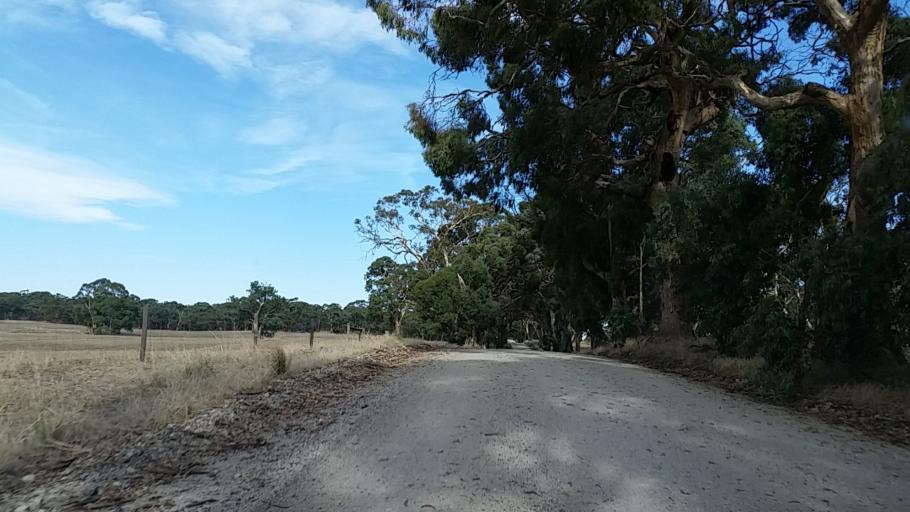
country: AU
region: South Australia
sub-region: Barossa
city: Angaston
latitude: -34.5748
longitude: 139.1268
